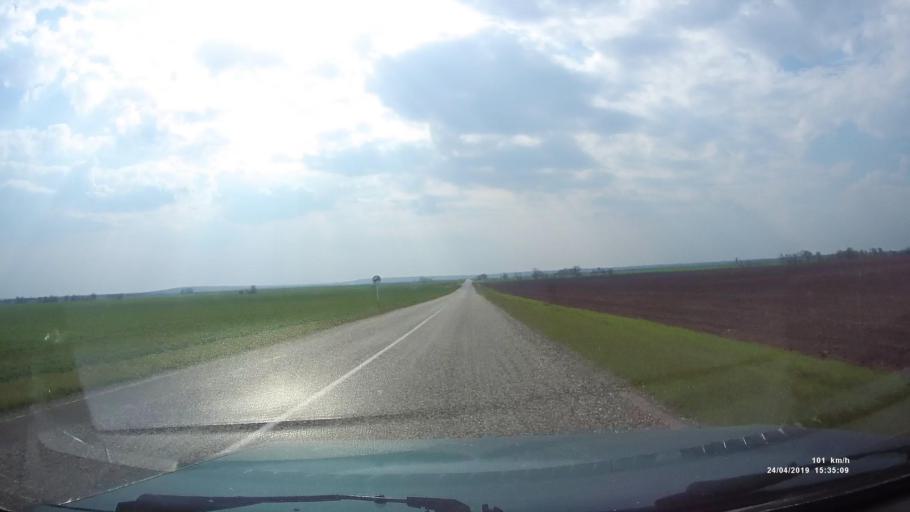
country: RU
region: Kalmykiya
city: Yashalta
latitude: 46.5994
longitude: 42.9000
